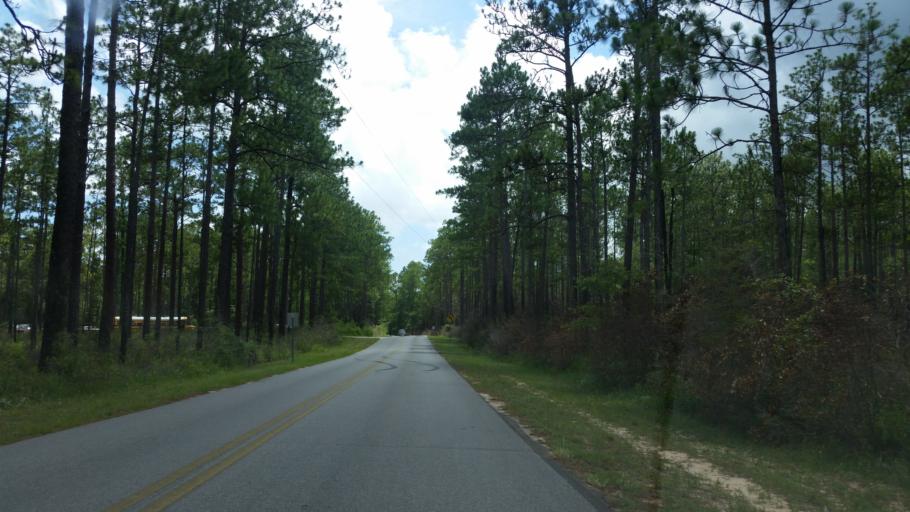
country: US
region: Florida
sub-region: Santa Rosa County
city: East Milton
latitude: 30.7095
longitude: -86.8817
